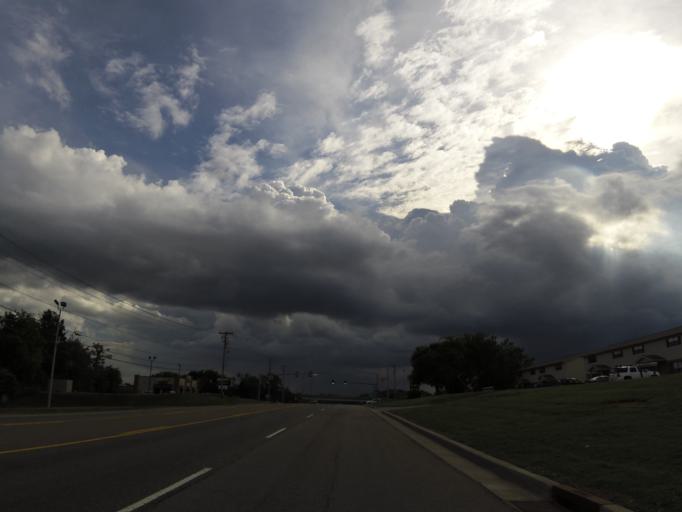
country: US
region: Tennessee
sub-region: Blount County
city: Alcoa
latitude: 35.8475
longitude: -83.9898
